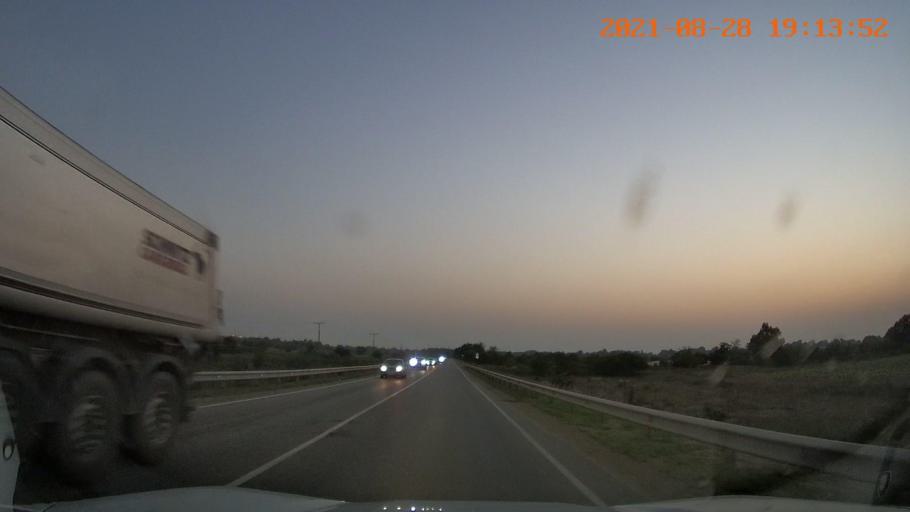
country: RU
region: Krasnodarskiy
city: Ryazanskaya
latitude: 44.9372
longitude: 39.5910
